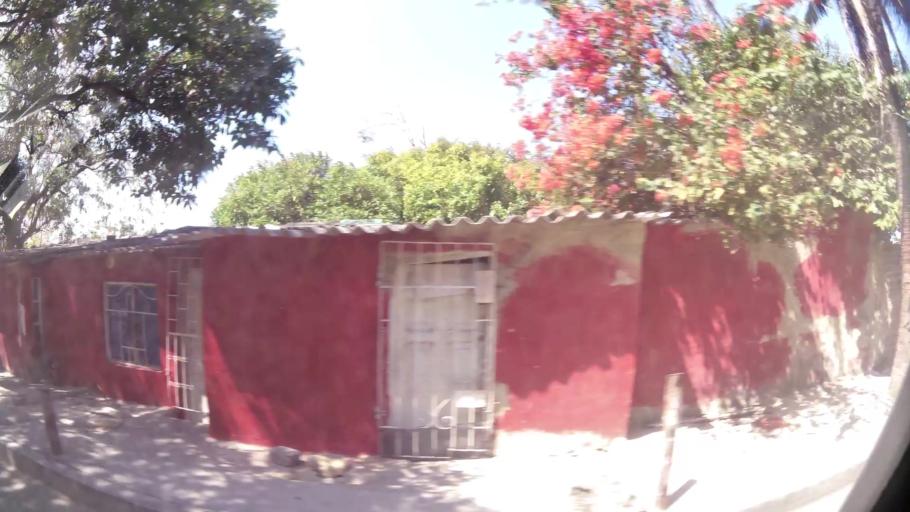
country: CO
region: Atlantico
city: Barranquilla
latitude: 10.9817
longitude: -74.8192
